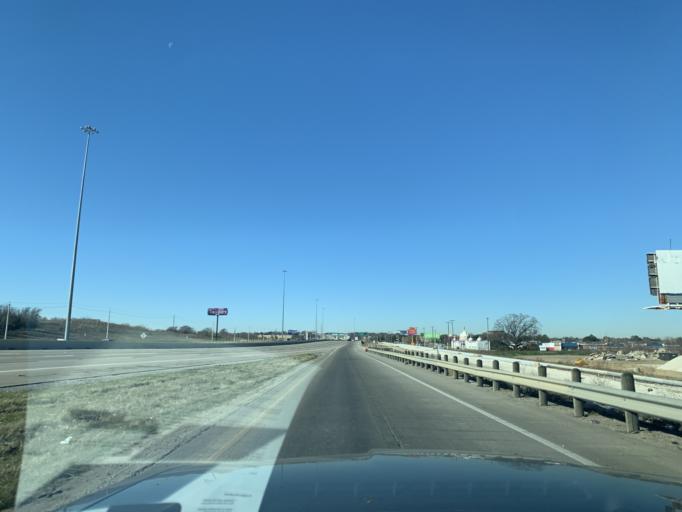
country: US
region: Texas
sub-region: Dallas County
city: Grand Prairie
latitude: 32.7592
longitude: -96.9989
